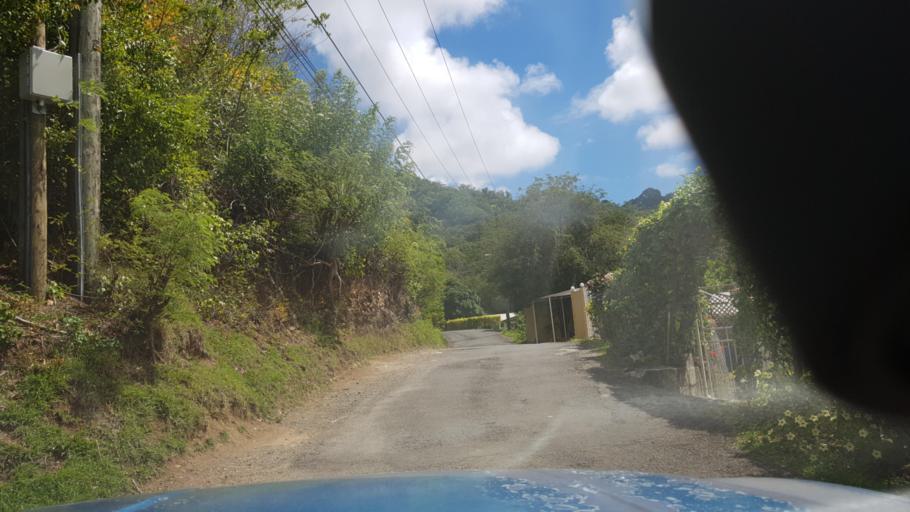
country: LC
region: Gros-Islet
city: Gros Islet
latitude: 14.0451
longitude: -60.9508
